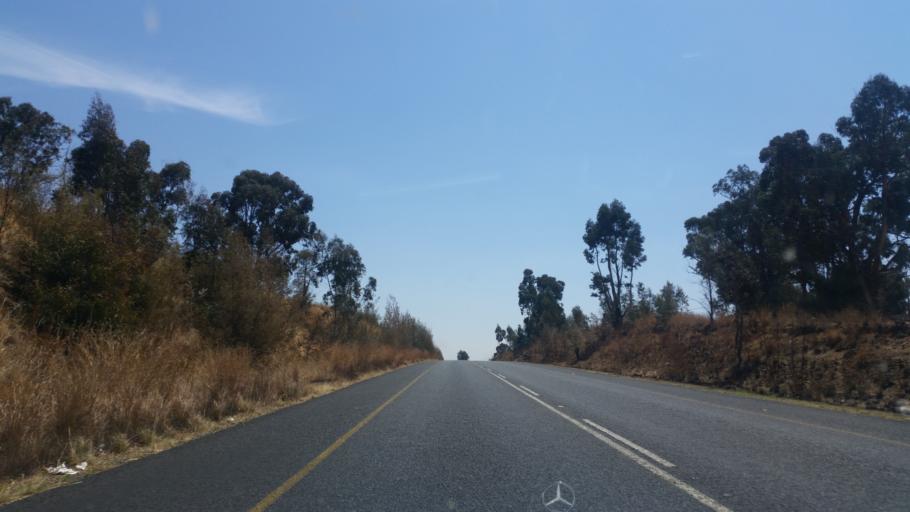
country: ZA
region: Orange Free State
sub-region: Thabo Mofutsanyana District Municipality
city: Phuthaditjhaba
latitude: -28.2292
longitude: 28.7041
